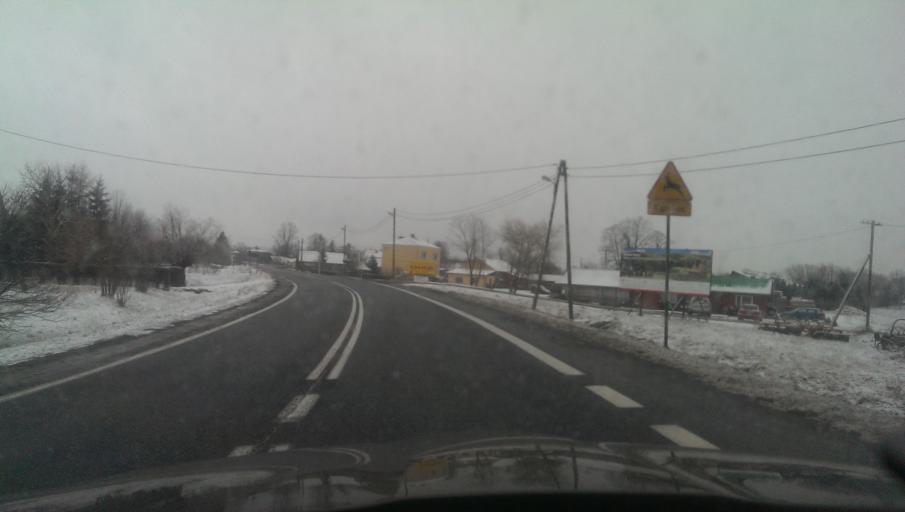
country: PL
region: Subcarpathian Voivodeship
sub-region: Powiat sanocki
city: Zarszyn
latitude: 49.5817
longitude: 22.0034
